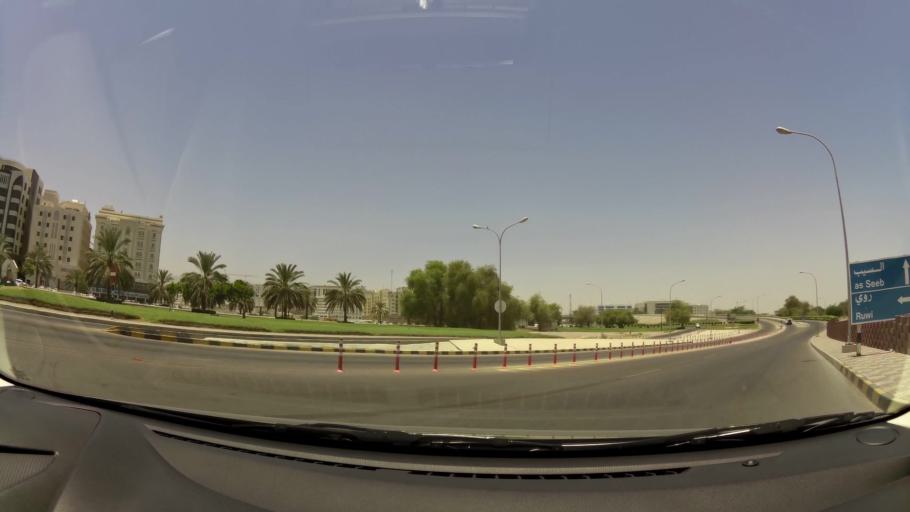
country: OM
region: Muhafazat Masqat
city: Bawshar
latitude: 23.5974
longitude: 58.4160
